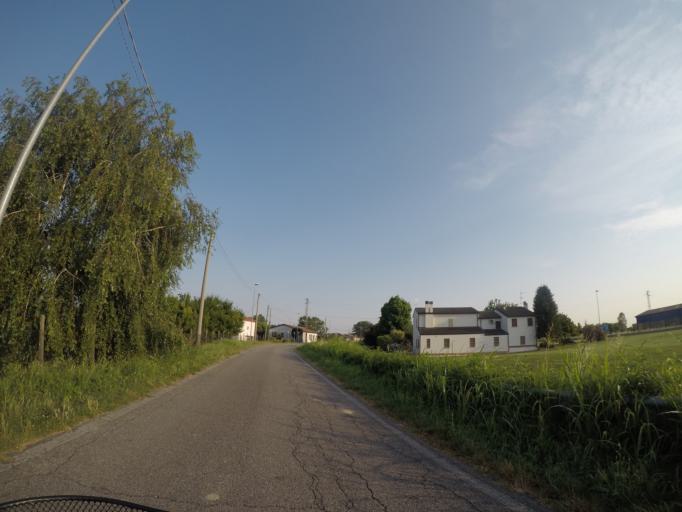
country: IT
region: Veneto
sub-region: Provincia di Rovigo
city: Fratta Polesine
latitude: 45.0243
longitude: 11.6409
